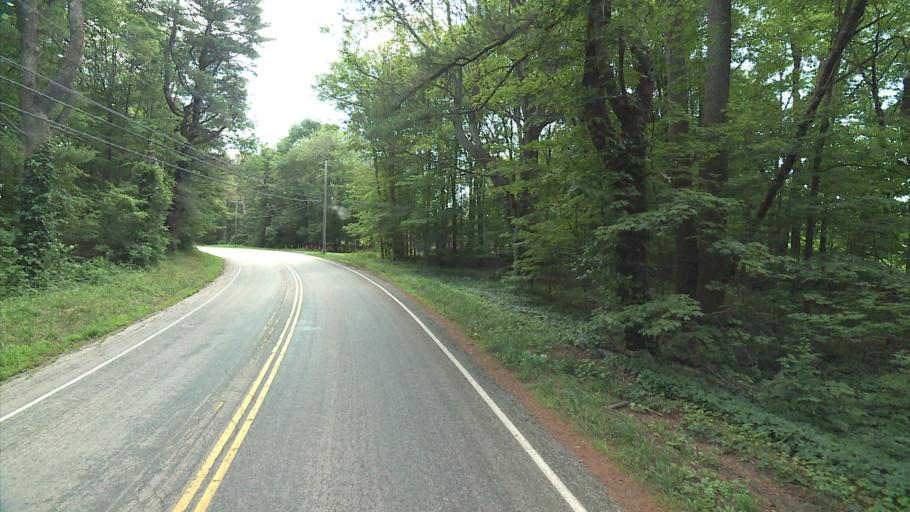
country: US
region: Connecticut
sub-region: Middlesex County
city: Moodus
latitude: 41.4707
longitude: -72.4117
